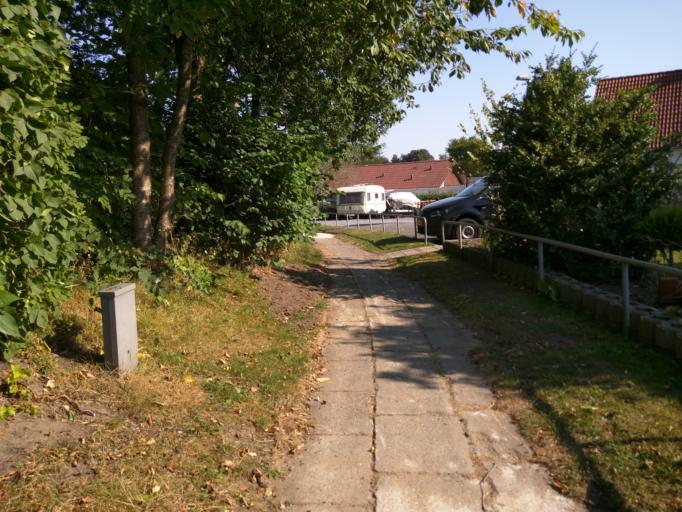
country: DK
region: Central Jutland
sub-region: Viborg Kommune
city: Viborg
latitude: 56.4330
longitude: 9.4000
